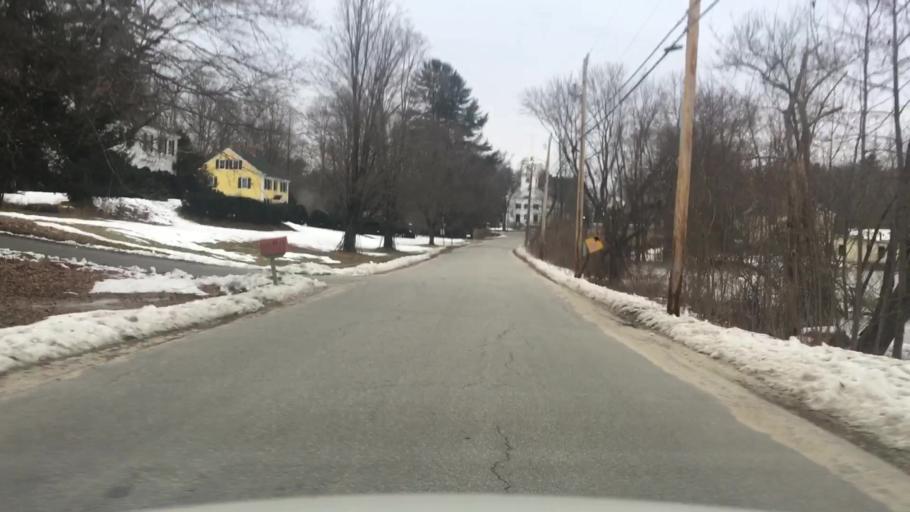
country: US
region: New Hampshire
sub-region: Merrimack County
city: Hopkinton
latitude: 43.1898
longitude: -71.6749
